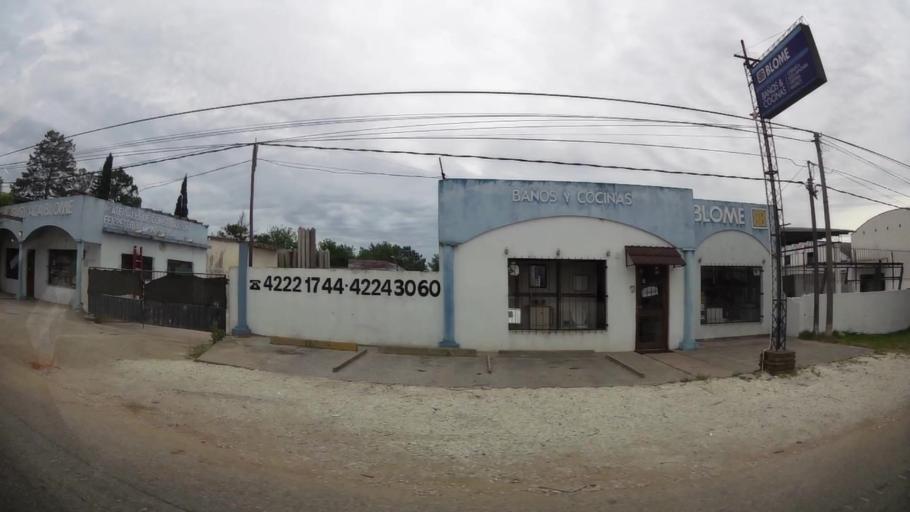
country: UY
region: Maldonado
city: Maldonado
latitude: -34.9116
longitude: -54.9424
